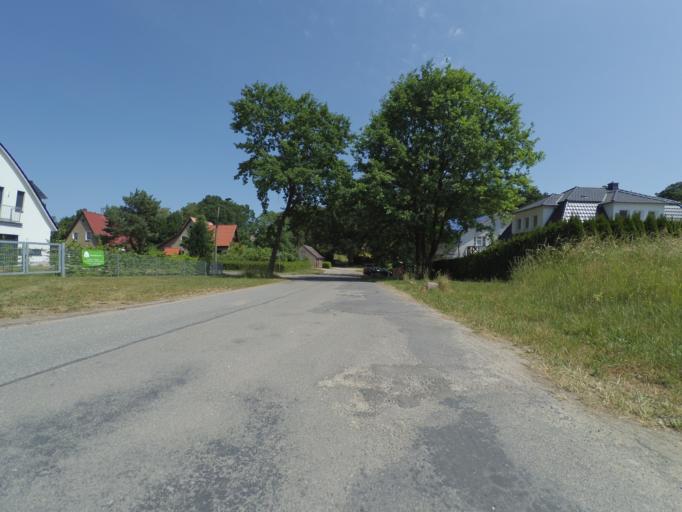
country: DE
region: Mecklenburg-Vorpommern
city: Plau am See
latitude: 53.4342
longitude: 12.2816
